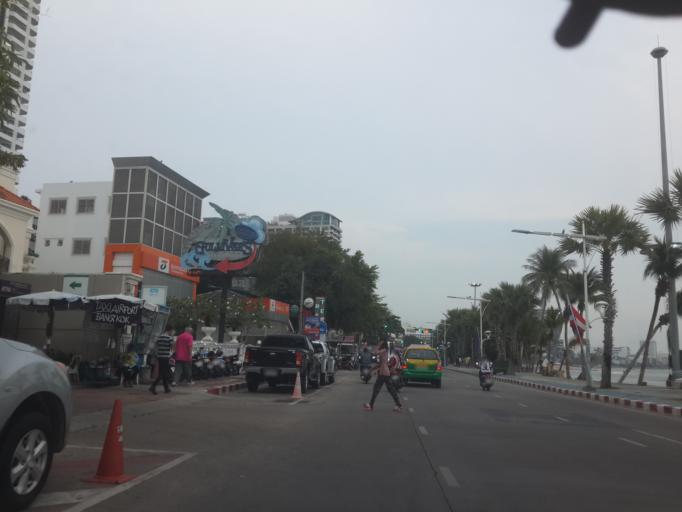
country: TH
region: Chon Buri
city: Phatthaya
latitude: 12.9477
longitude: 100.8847
